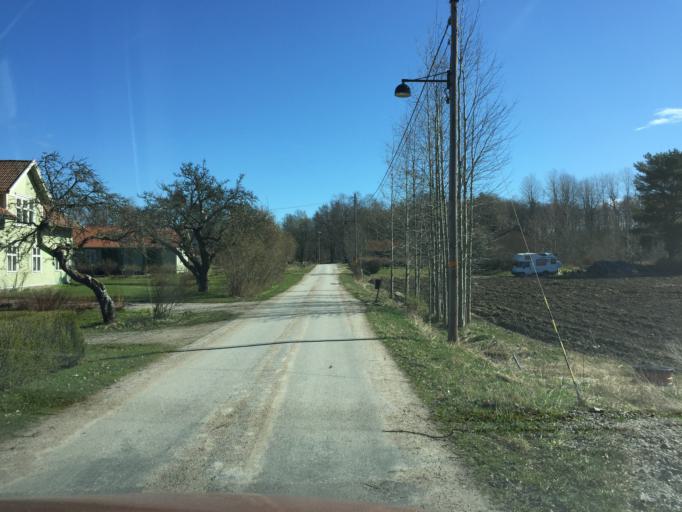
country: SE
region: OEstergoetland
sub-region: Finspangs Kommun
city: Finspang
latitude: 58.8928
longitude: 15.6964
